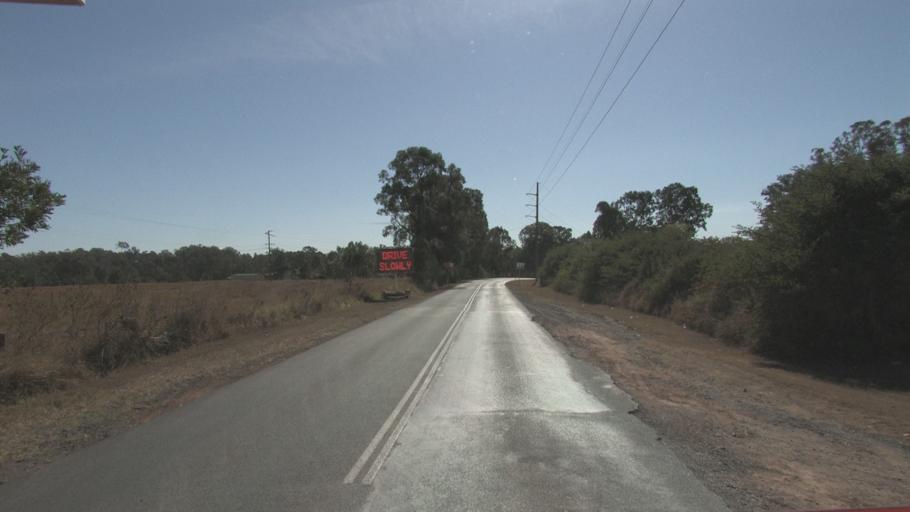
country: AU
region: Queensland
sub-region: Logan
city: Cedar Vale
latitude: -27.8631
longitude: 153.0179
